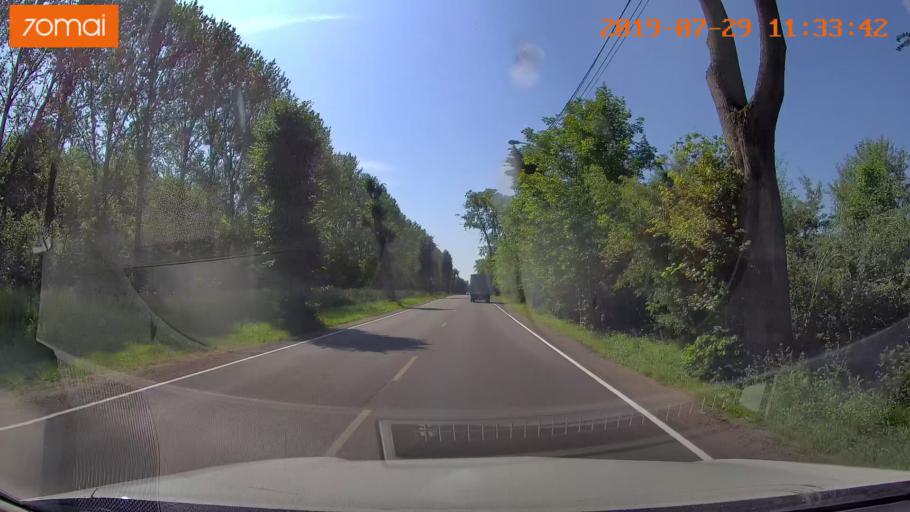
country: RU
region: Kaliningrad
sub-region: Gorod Kaliningrad
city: Kaliningrad
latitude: 54.6624
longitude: 20.5406
